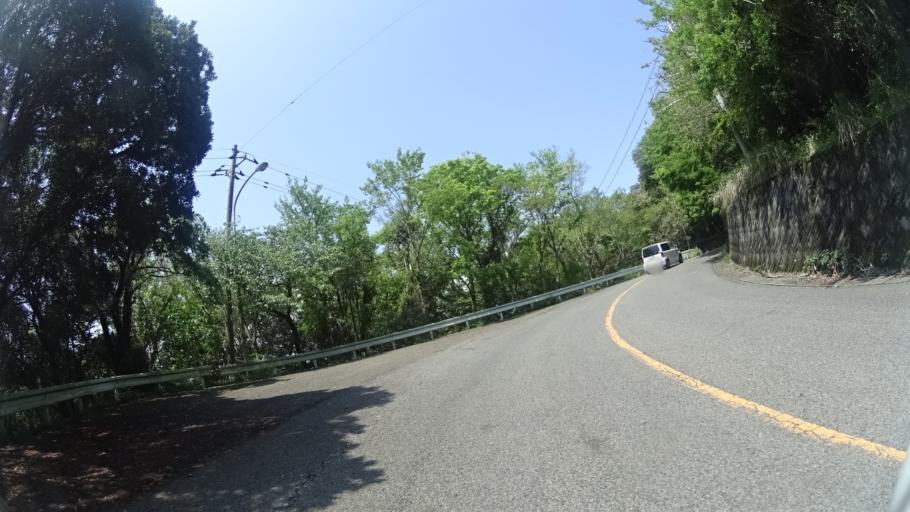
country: JP
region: Tokushima
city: Tokushima-shi
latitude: 34.0658
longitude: 134.5327
